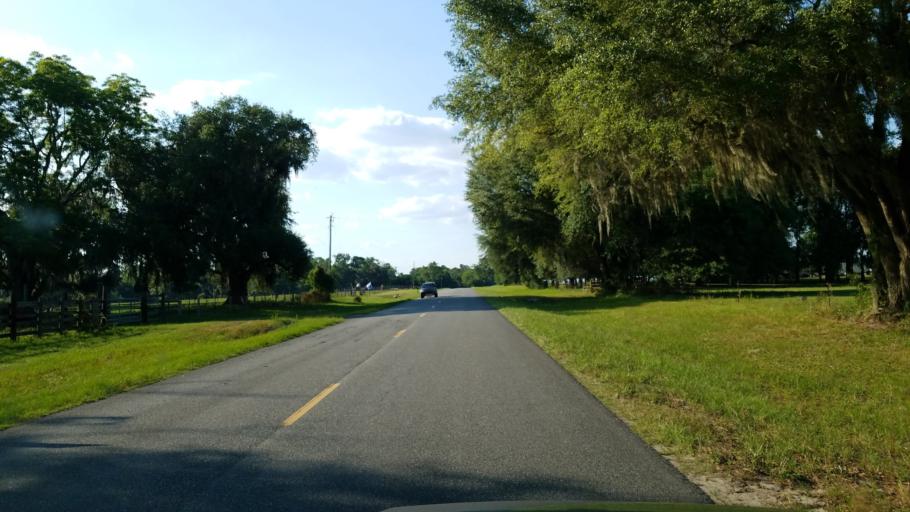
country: US
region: Georgia
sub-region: Echols County
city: Statenville
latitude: 30.6145
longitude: -83.0959
